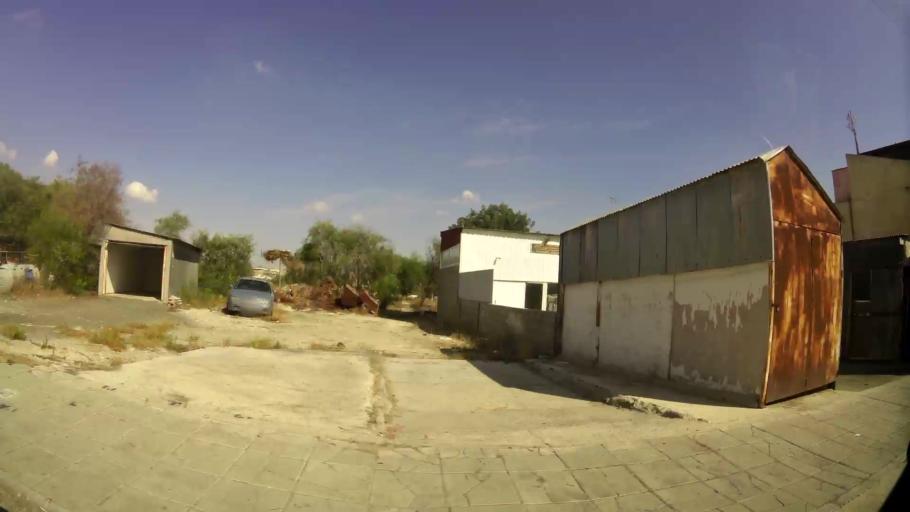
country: CY
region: Larnaka
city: Aradippou
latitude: 34.9526
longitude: 33.5845
